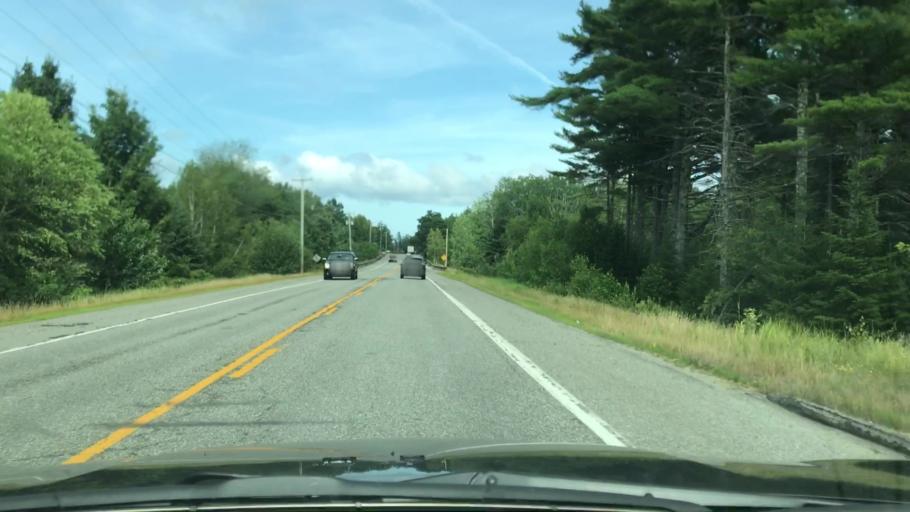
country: US
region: Maine
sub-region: Hancock County
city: Trenton
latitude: 44.4188
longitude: -68.3415
